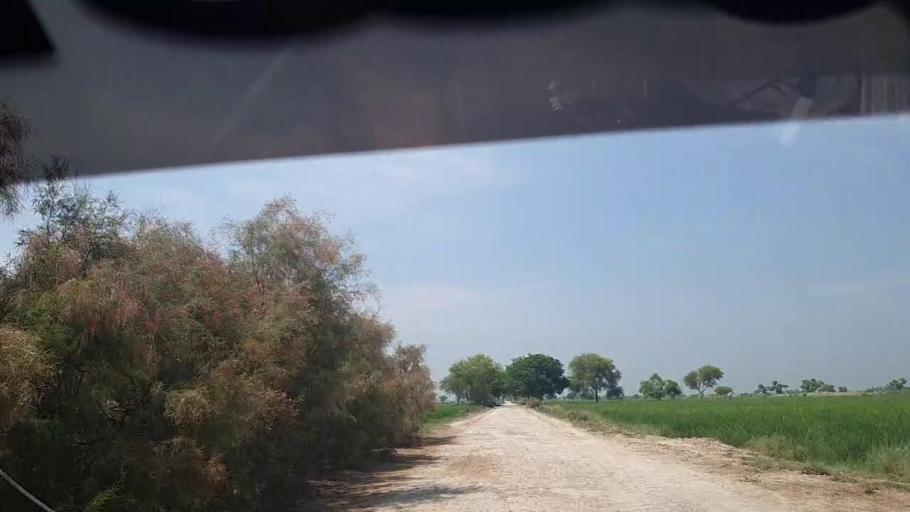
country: PK
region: Sindh
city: Thul
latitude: 28.1726
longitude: 68.7483
